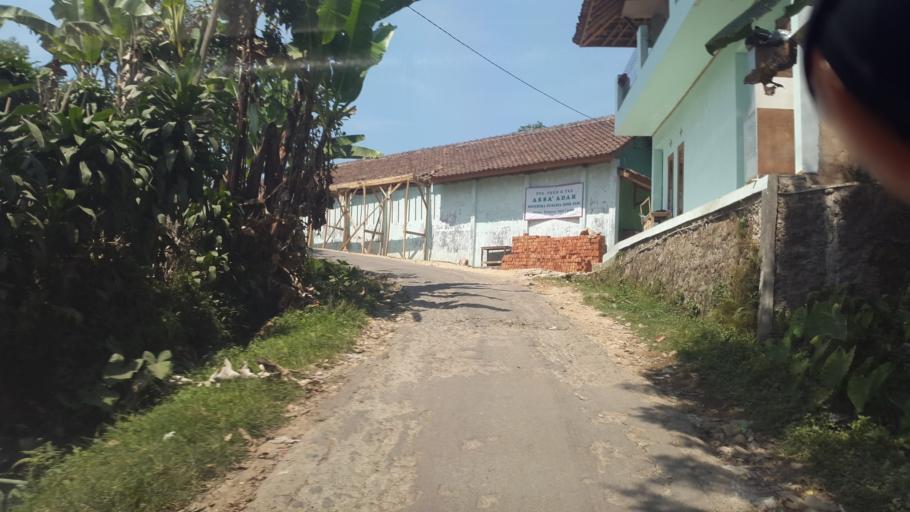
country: ID
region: West Java
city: Cicurug
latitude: -6.8024
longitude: 106.6701
